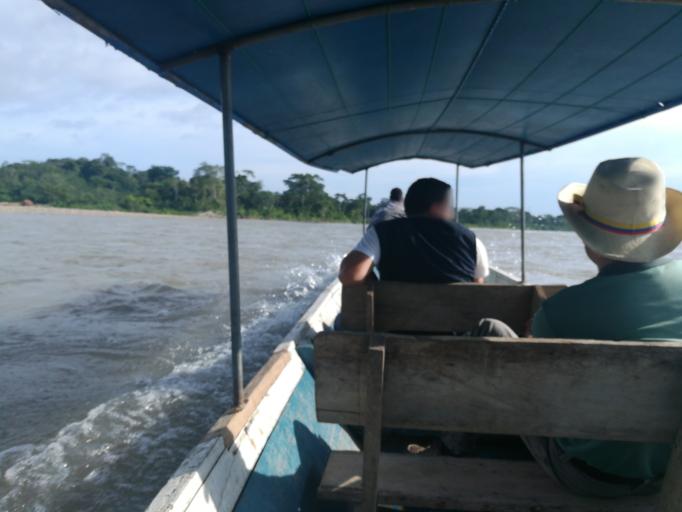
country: EC
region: Orellana
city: Boca Suno
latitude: -0.8338
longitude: -77.1945
